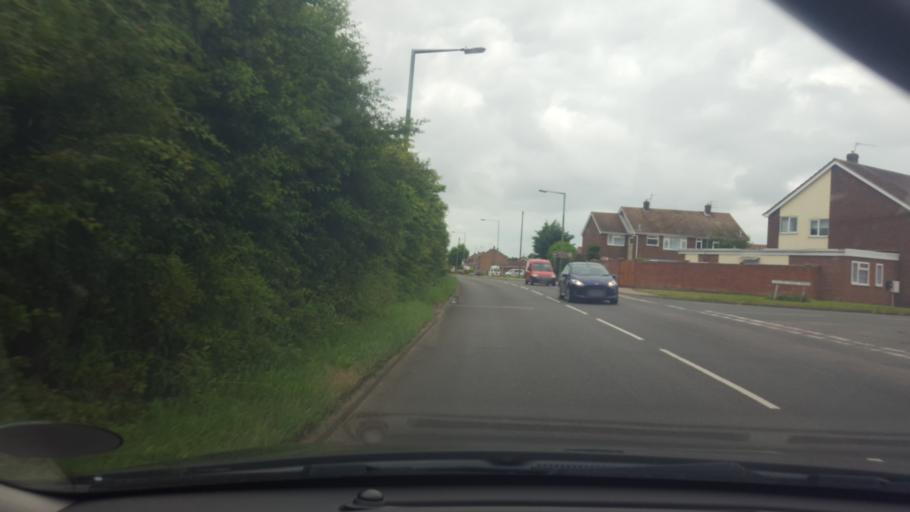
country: GB
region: England
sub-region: Essex
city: Clacton-on-Sea
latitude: 51.7868
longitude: 1.1198
